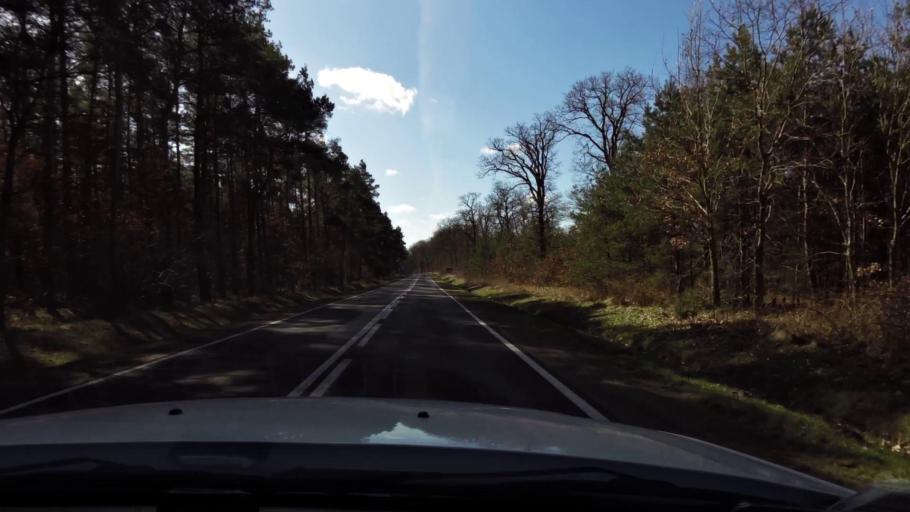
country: PL
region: West Pomeranian Voivodeship
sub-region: Powiat gryfinski
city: Gryfino
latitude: 53.2079
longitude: 14.4810
